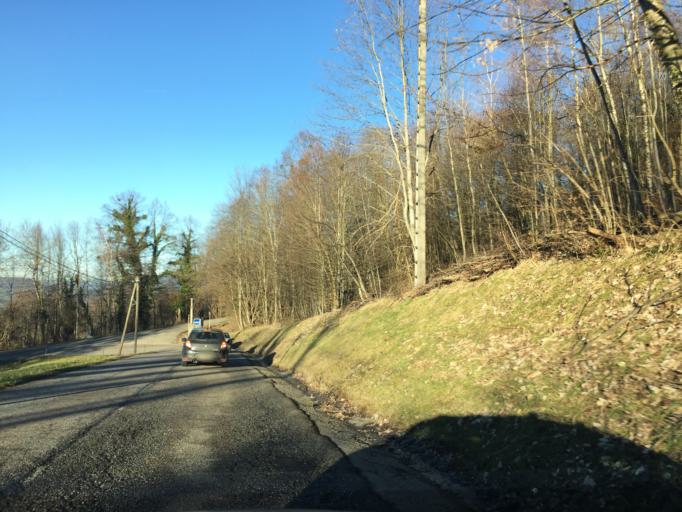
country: FR
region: Rhone-Alpes
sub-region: Departement de la Savoie
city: Gresy-sur-Aix
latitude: 45.7057
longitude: 5.9711
